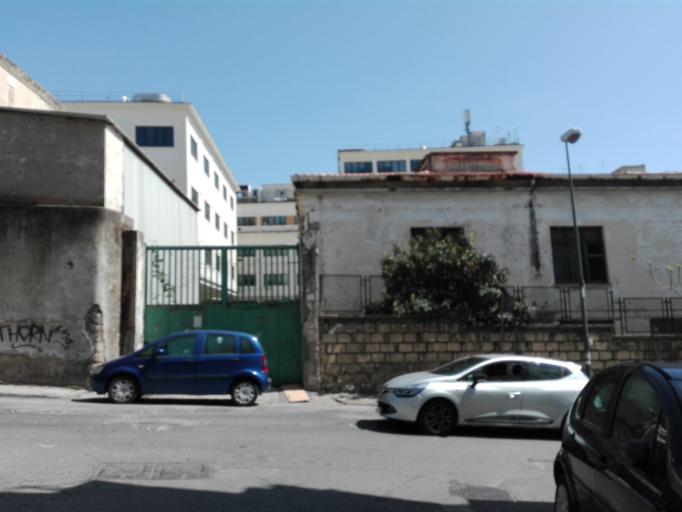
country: IT
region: Campania
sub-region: Provincia di Napoli
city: Napoli
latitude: 40.8547
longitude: 14.2237
